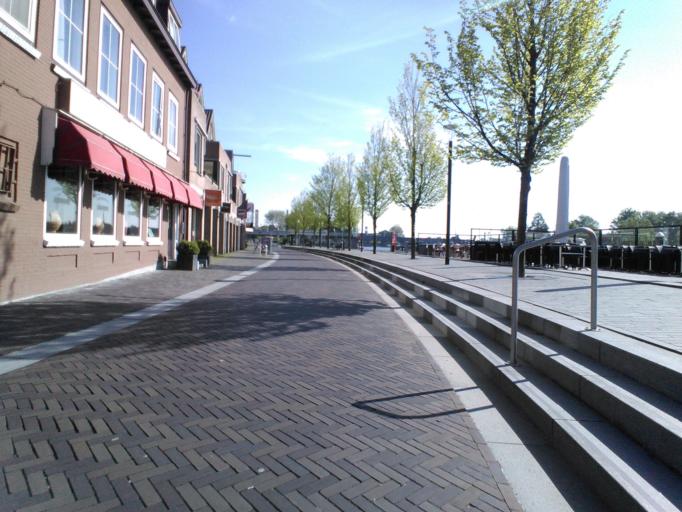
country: NL
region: North Holland
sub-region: Gemeente Uithoorn
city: Uithoorn
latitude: 52.2333
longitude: 4.8345
